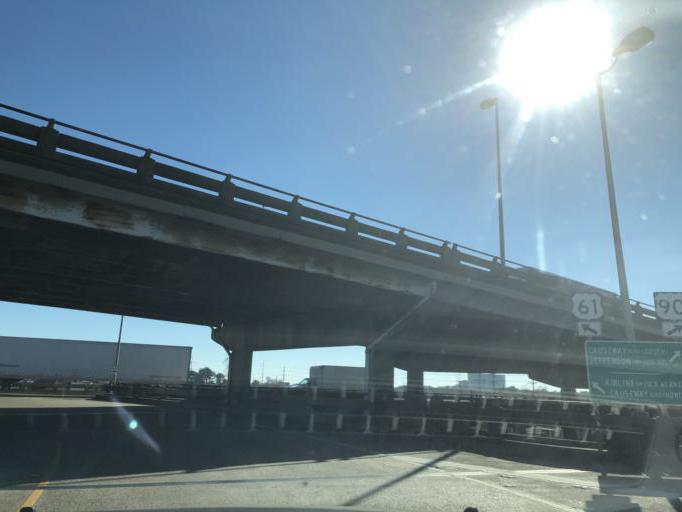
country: US
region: Louisiana
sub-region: Jefferson Parish
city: Metairie Terrace
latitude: 29.9744
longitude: -90.1568
